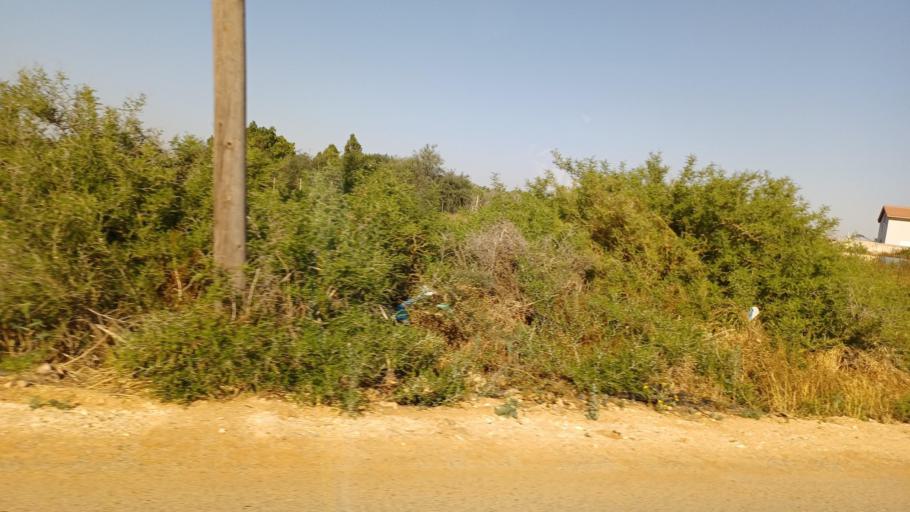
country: CY
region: Ammochostos
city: Frenaros
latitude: 35.0521
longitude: 33.9156
